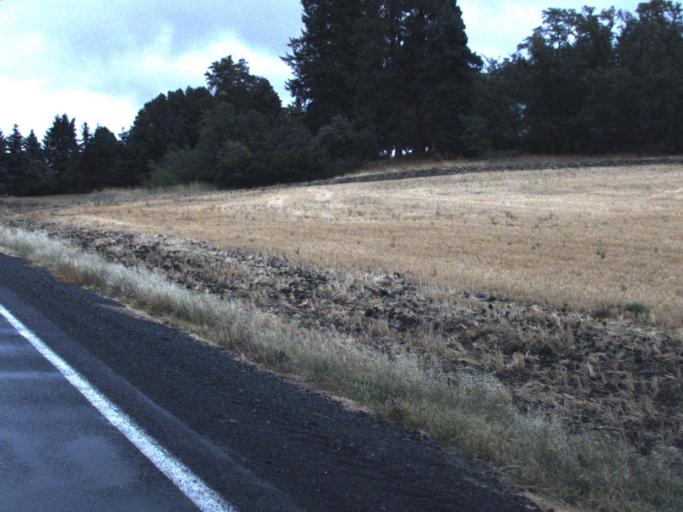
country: US
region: Washington
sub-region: Whitman County
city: Colfax
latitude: 47.0024
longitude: -117.4315
